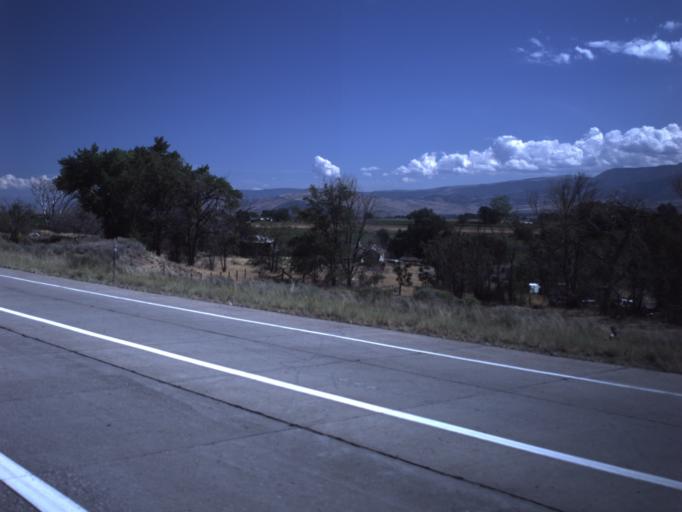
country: US
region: Utah
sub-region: Sevier County
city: Monroe
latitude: 38.6903
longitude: -112.1508
